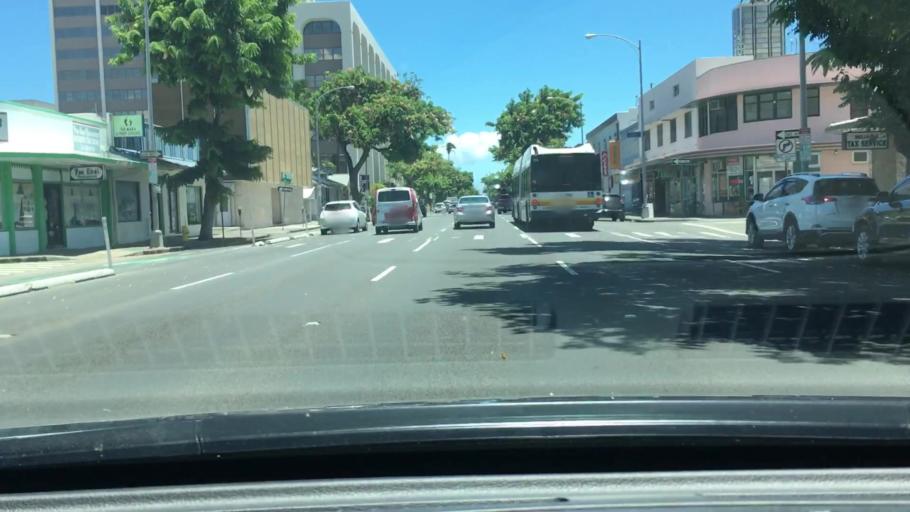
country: US
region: Hawaii
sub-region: Honolulu County
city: Honolulu
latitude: 21.2994
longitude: -157.8430
